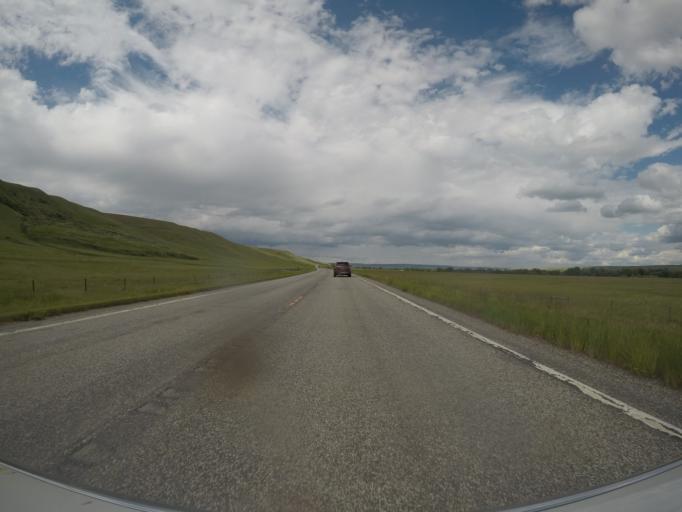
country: US
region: Montana
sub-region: Sweet Grass County
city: Big Timber
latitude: 45.7937
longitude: -109.9727
